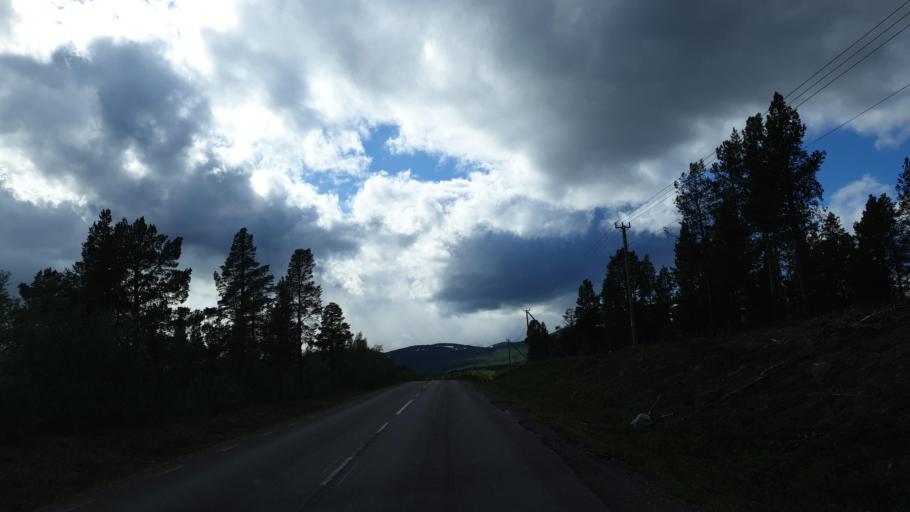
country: SE
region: Norrbotten
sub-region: Kiruna Kommun
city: Kiruna
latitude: 67.8695
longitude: 19.2587
